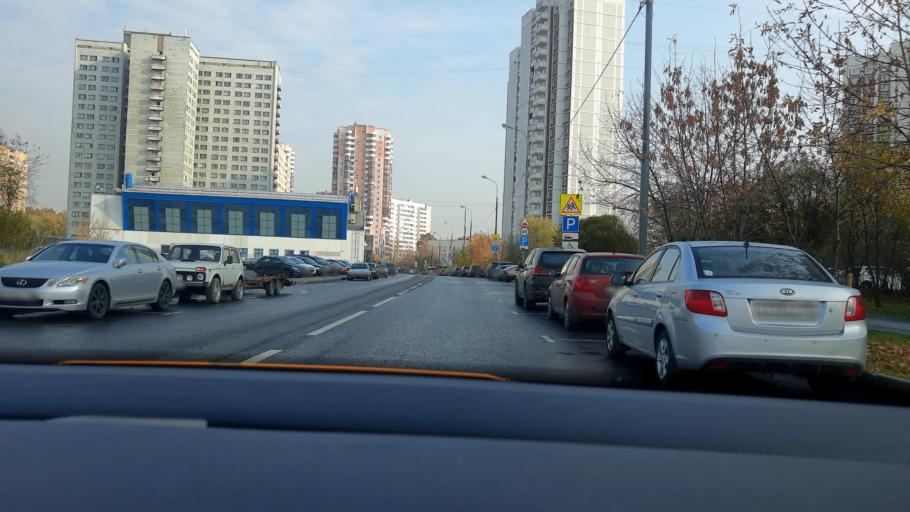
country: RU
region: Moscow
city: Khimki
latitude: 55.8619
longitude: 37.4167
